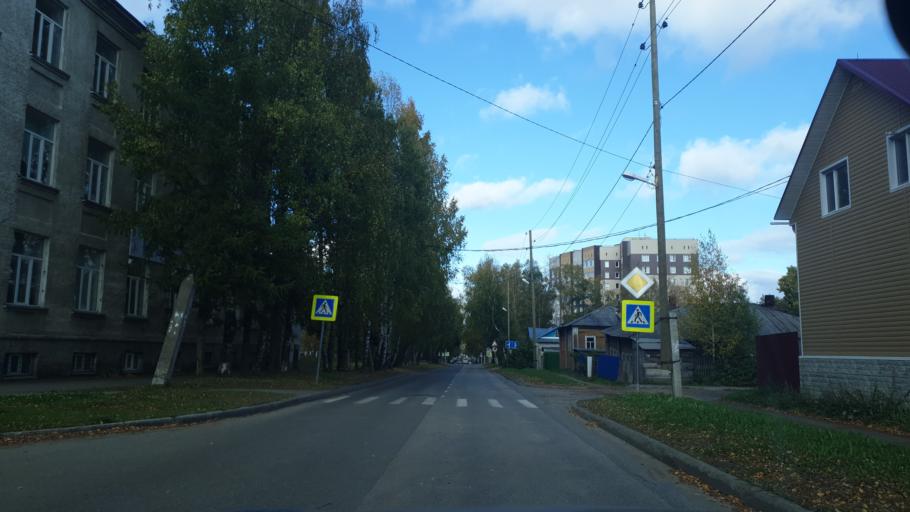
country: RU
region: Komi Republic
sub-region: Syktyvdinskiy Rayon
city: Syktyvkar
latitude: 61.6612
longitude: 50.8405
